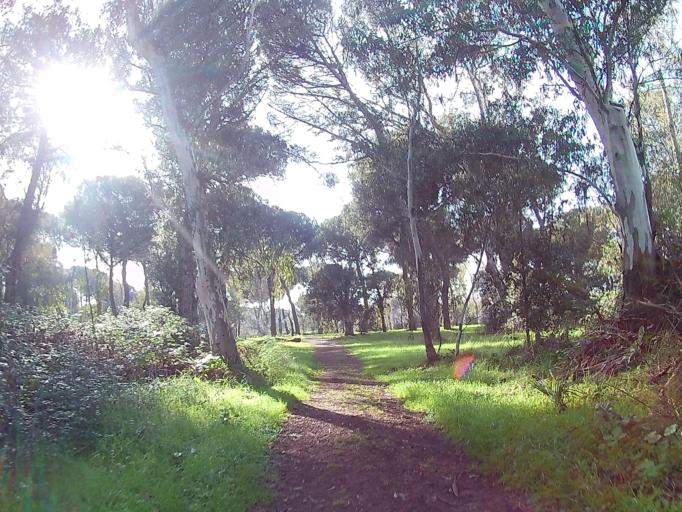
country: IT
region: Latium
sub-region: Citta metropolitana di Roma Capitale
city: Lido di Ostia
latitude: 41.7450
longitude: 12.2712
